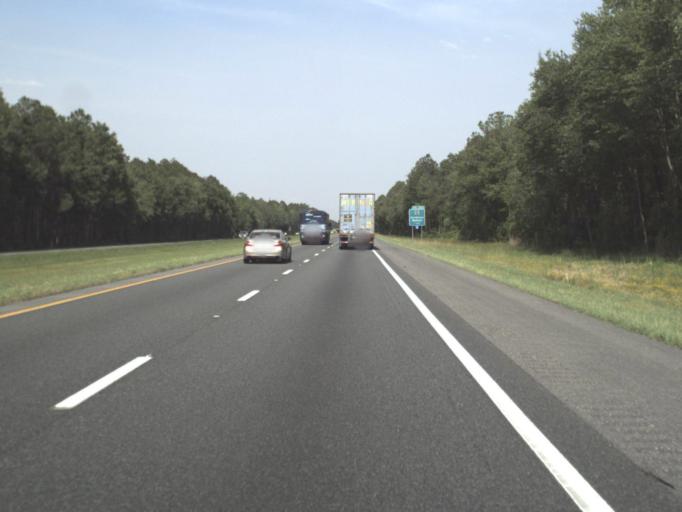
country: US
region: Florida
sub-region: Baker County
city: Macclenny
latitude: 30.2357
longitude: -82.2769
